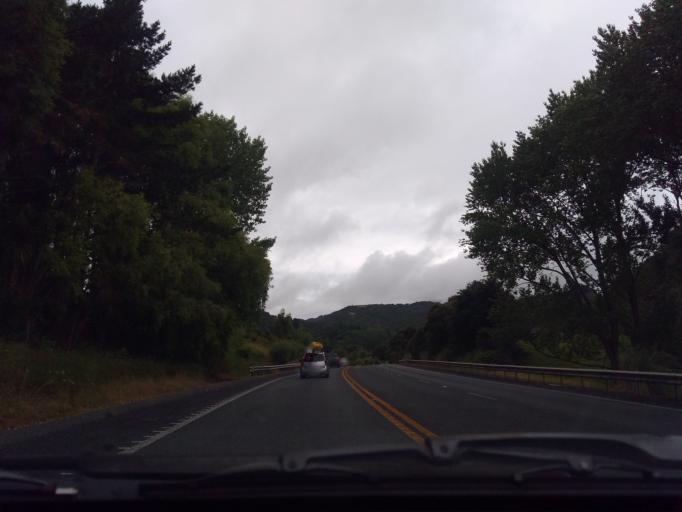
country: NZ
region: Auckland
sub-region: Auckland
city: Wellsford
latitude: -36.1321
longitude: 174.4298
